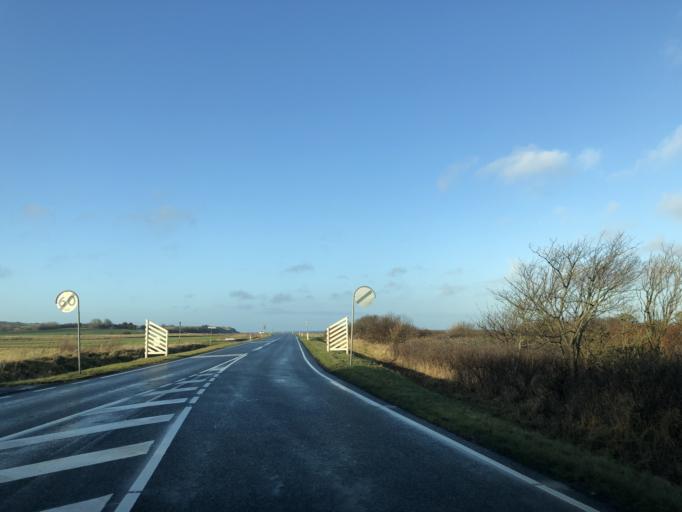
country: DK
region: Central Jutland
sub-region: Struer Kommune
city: Struer
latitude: 56.5557
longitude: 8.4745
